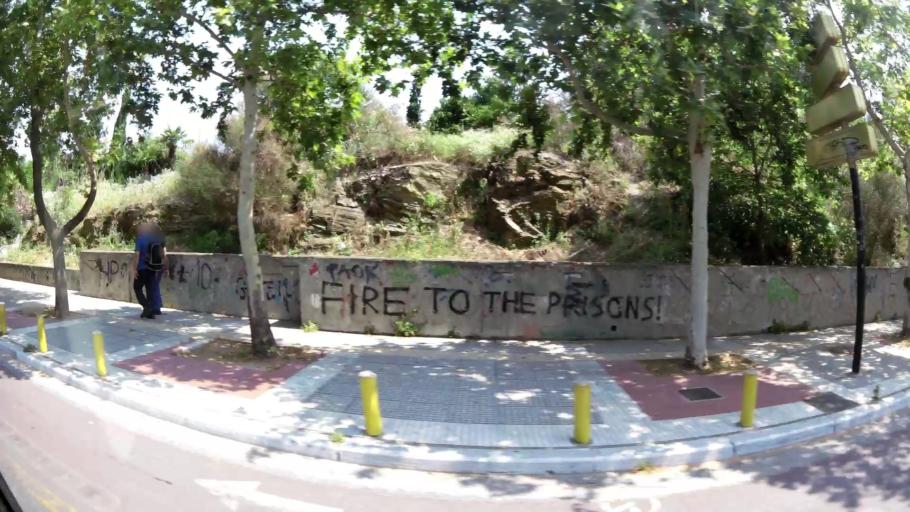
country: GR
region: Central Macedonia
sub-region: Nomos Thessalonikis
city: Agios Pavlos
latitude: 40.6337
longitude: 22.9577
